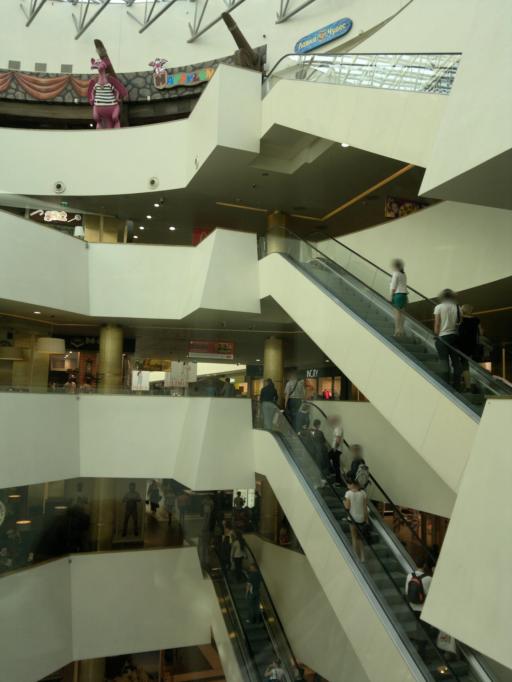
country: RU
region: St.-Petersburg
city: Centralniy
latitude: 59.9283
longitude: 30.3606
